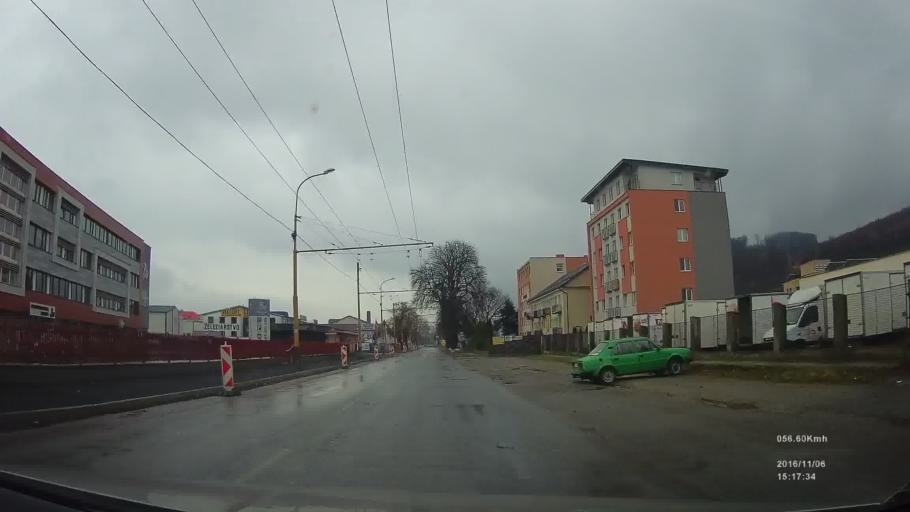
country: SK
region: Presovsky
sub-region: Okres Presov
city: Presov
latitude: 48.9789
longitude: 21.2441
